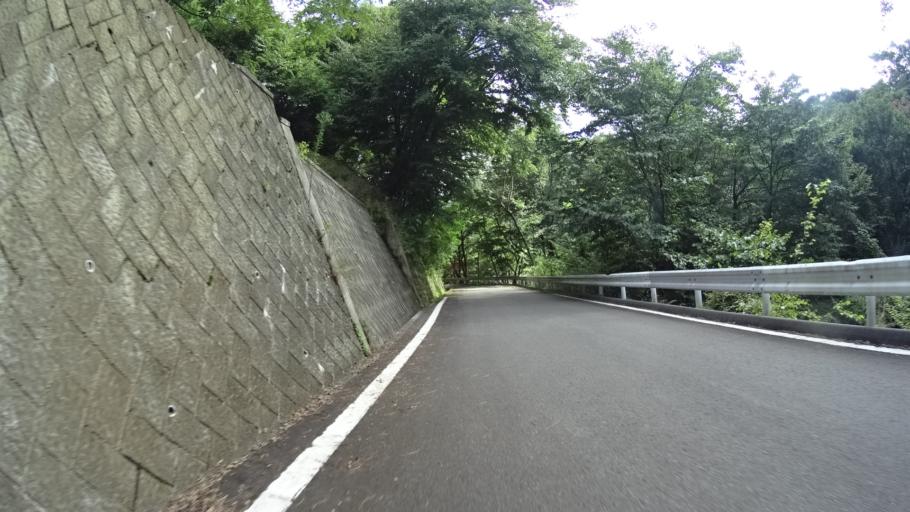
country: JP
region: Yamanashi
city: Enzan
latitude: 35.6125
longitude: 138.7878
